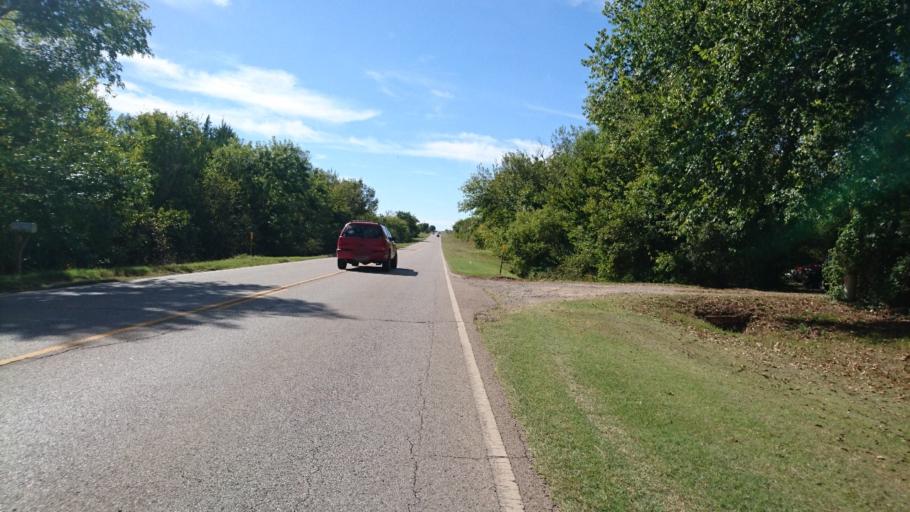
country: US
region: Oklahoma
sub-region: Lincoln County
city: Chandler
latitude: 35.7099
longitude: -96.7761
